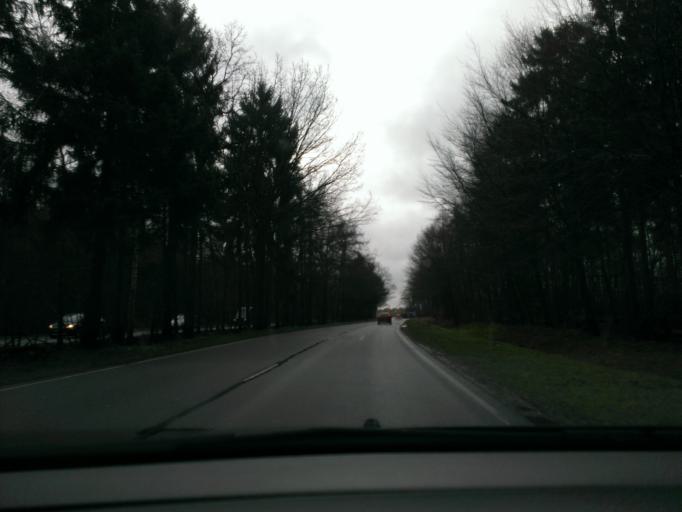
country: NL
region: Drenthe
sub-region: Gemeente Coevorden
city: Sleen
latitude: 52.7621
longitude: 6.8510
